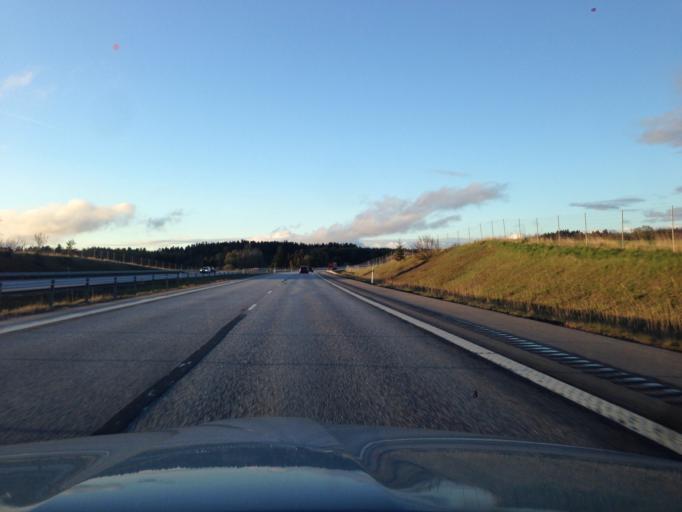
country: SE
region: Soedermanland
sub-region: Trosa Kommun
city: Vagnharad
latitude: 58.9483
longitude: 17.4347
